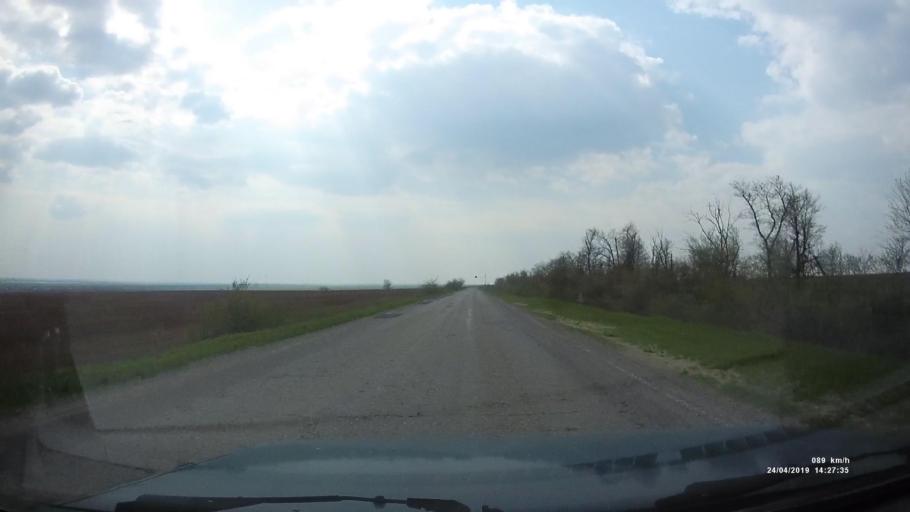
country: RU
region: Kalmykiya
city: Arshan'
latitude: 46.3339
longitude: 44.0401
